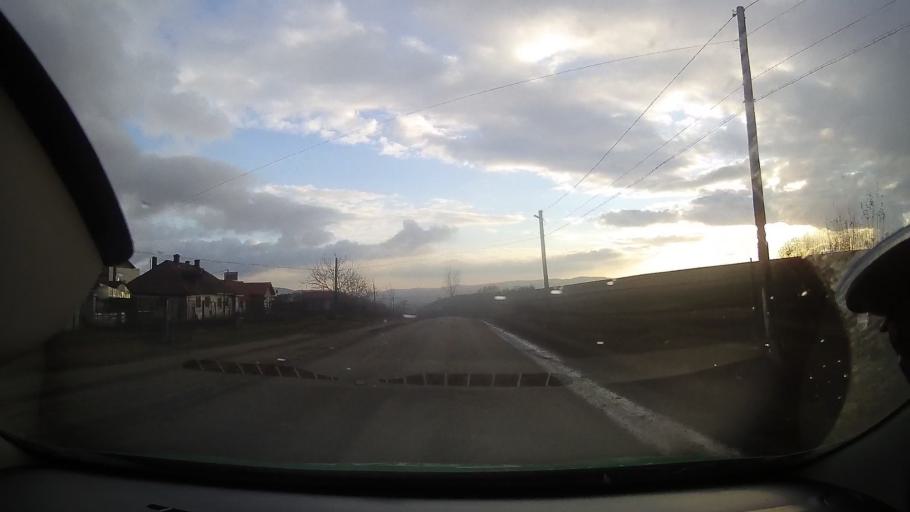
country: RO
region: Alba
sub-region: Comuna Lunca Muresului
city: Lunca Muresului
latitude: 46.4382
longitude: 23.9089
